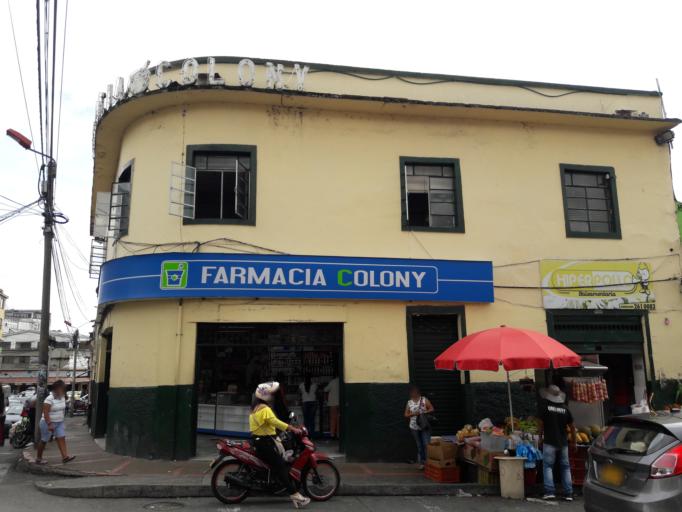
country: CO
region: Tolima
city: Ibague
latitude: 4.4412
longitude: -75.2403
